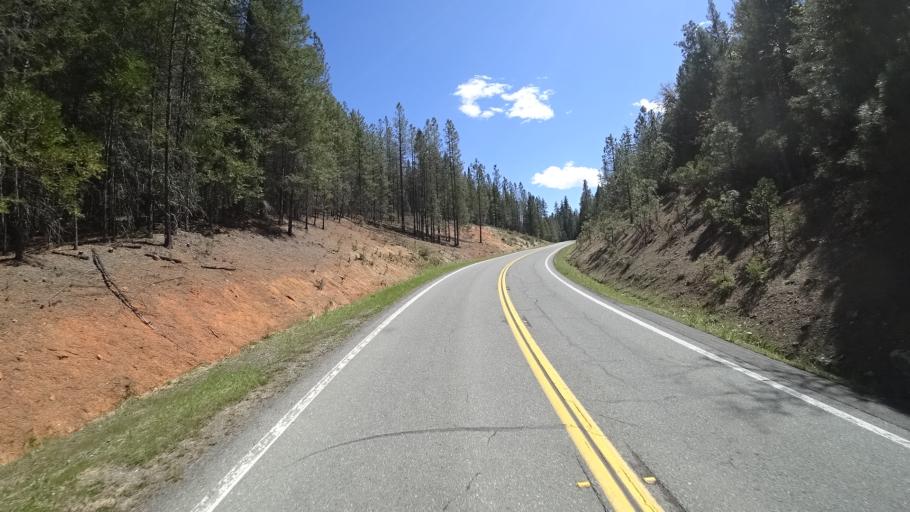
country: US
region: California
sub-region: Trinity County
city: Lewiston
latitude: 40.8630
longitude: -122.8172
